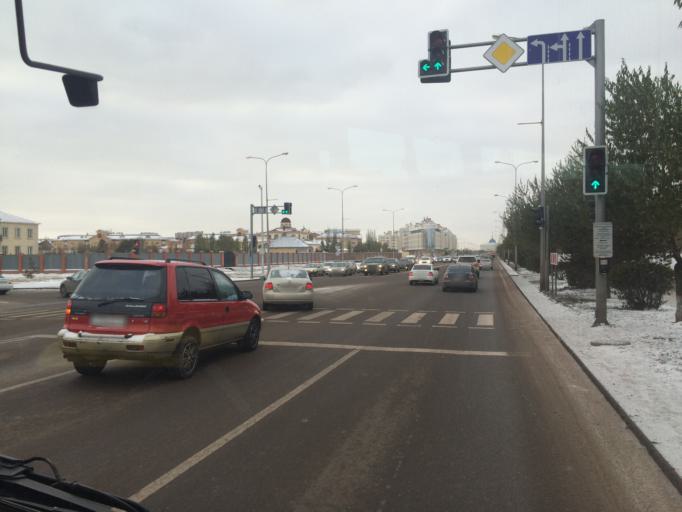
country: KZ
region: Astana Qalasy
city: Astana
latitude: 51.1488
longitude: 71.4446
